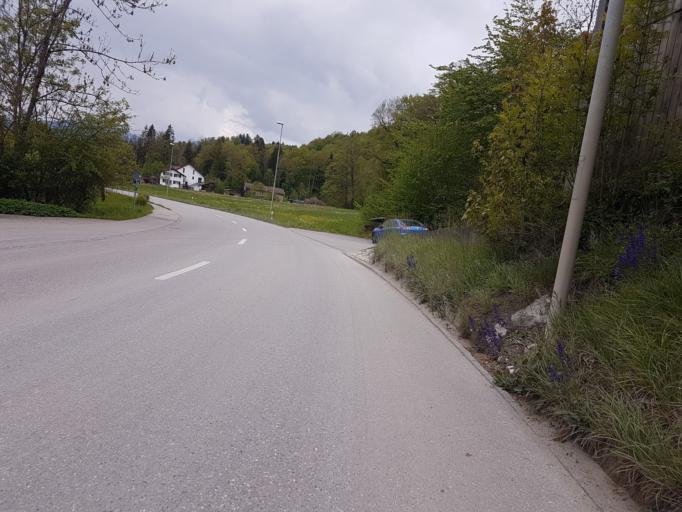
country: CH
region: Bern
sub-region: Oberaargau
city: Oberbipp
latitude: 47.2374
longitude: 7.6834
